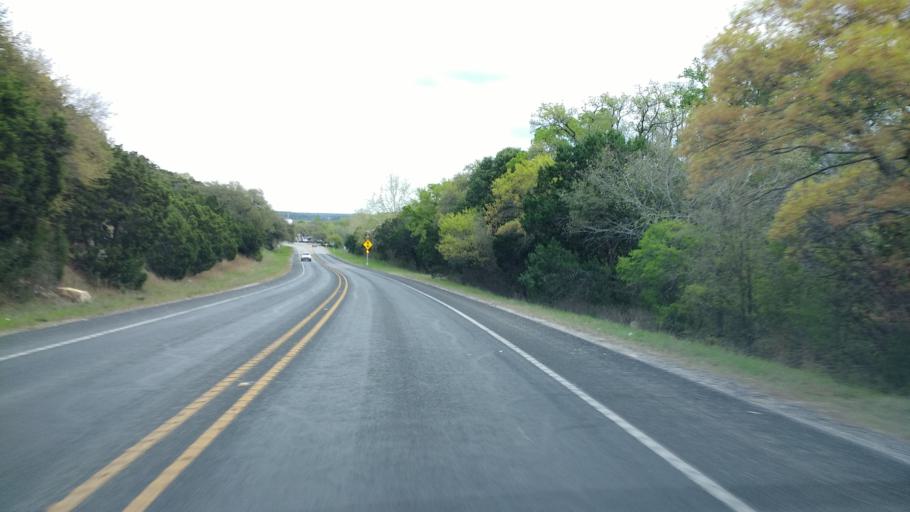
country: US
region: Texas
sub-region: Comal County
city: Canyon Lake
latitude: 29.8795
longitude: -98.1985
